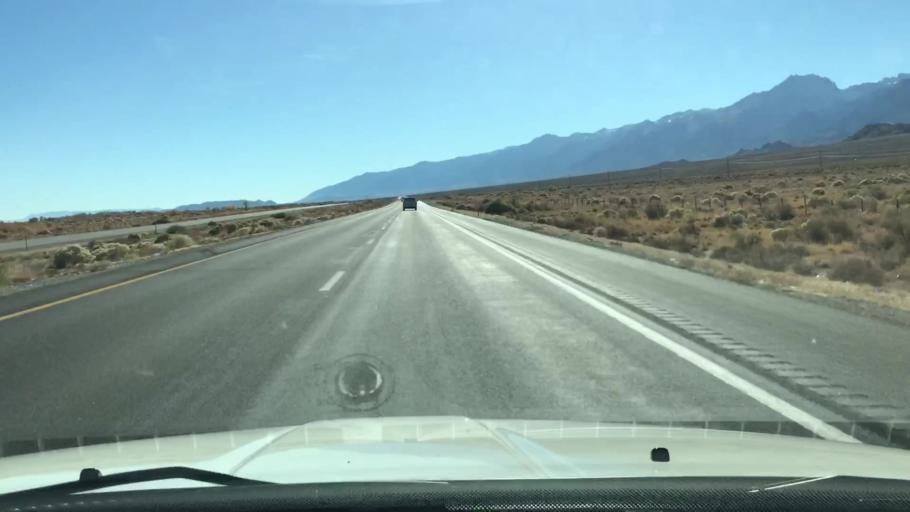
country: US
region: California
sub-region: Inyo County
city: Big Pine
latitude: 36.8873
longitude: -118.2414
